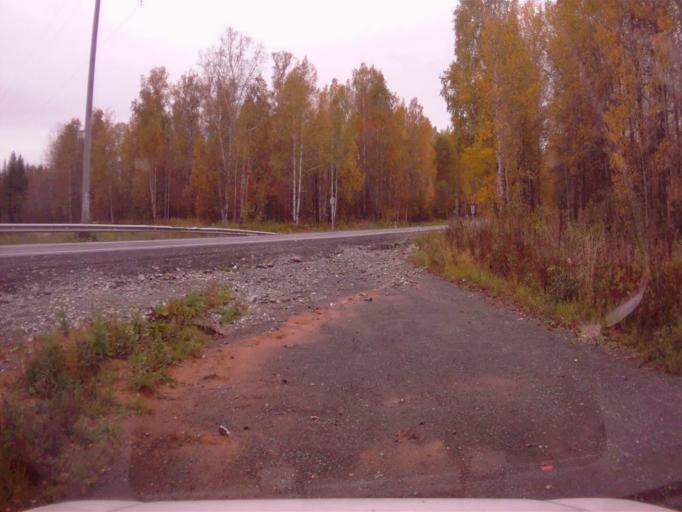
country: RU
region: Chelyabinsk
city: Nyazepetrovsk
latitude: 56.0663
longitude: 59.6461
